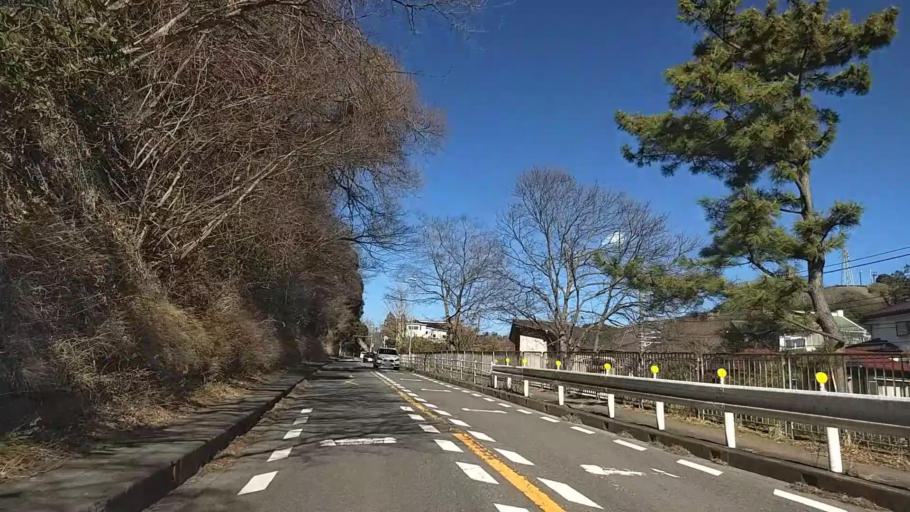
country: JP
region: Kanagawa
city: Zushi
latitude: 35.3236
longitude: 139.5814
